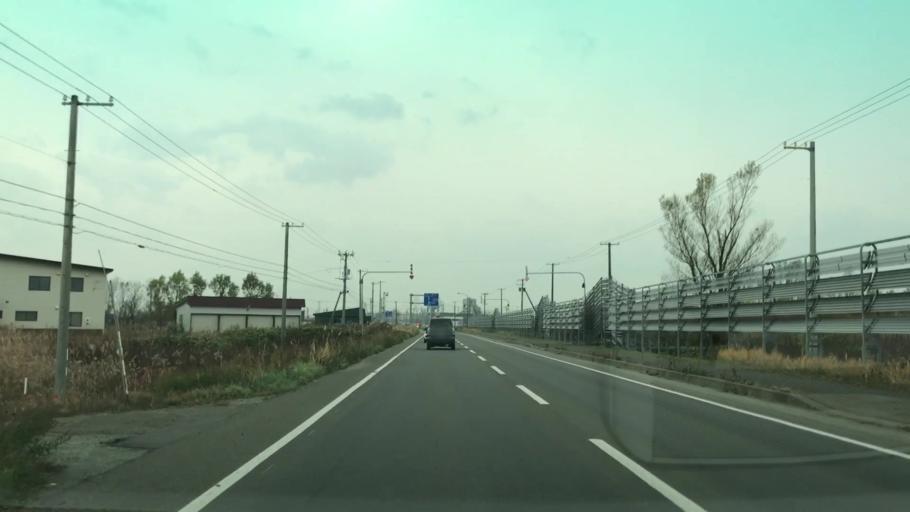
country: JP
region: Hokkaido
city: Ishikari
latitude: 43.2193
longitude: 141.3404
